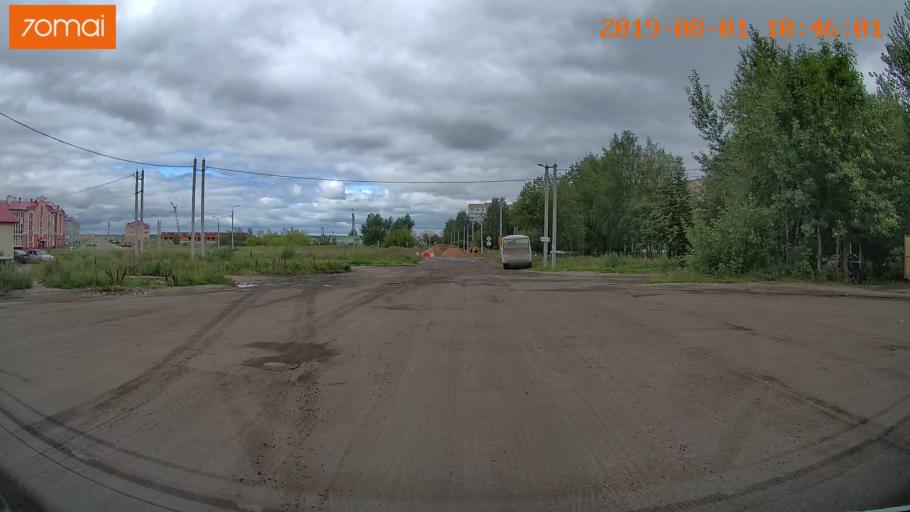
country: RU
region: Ivanovo
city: Kokhma
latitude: 56.9530
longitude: 41.1083
